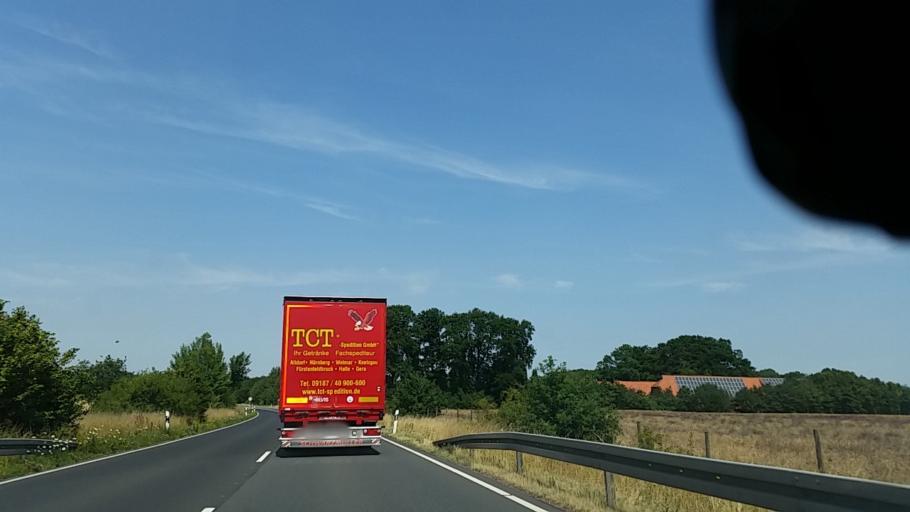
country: DE
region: Lower Saxony
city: Wietzen
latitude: 52.6735
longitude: 9.1060
